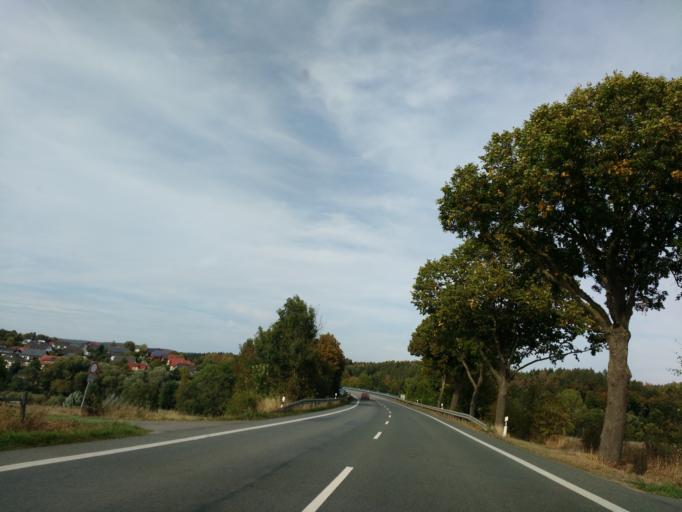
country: DE
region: North Rhine-Westphalia
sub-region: Regierungsbezirk Detmold
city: Willebadessen
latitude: 51.6203
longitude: 9.1382
